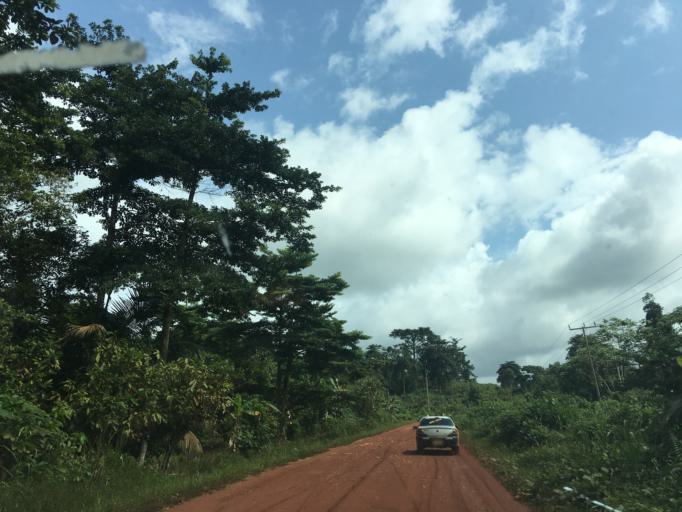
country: GH
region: Western
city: Wassa-Akropong
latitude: 5.7853
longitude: -2.3899
